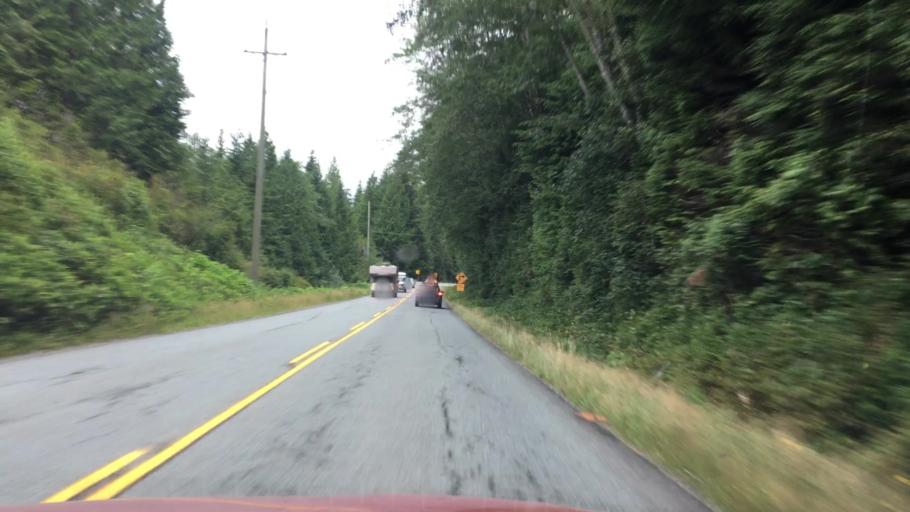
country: CA
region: British Columbia
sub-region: Regional District of Alberni-Clayoquot
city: Ucluelet
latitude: 49.0889
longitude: -125.4570
